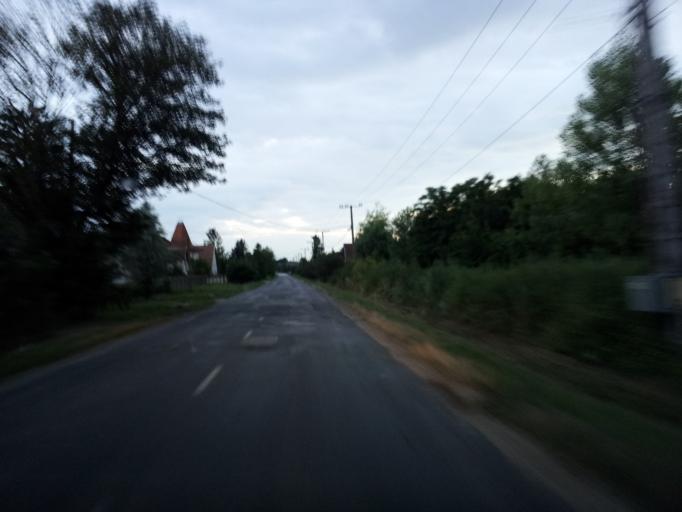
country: HU
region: Somogy
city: Adand
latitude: 46.8407
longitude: 18.1112
